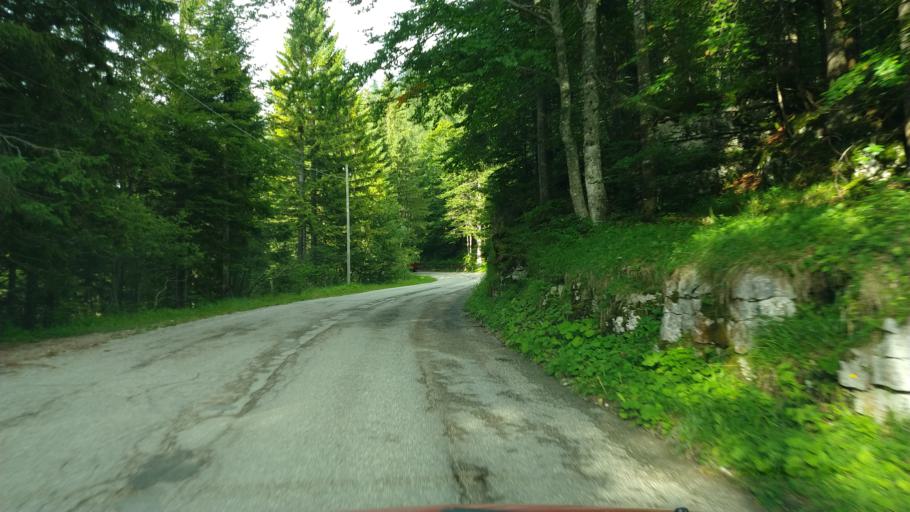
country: IT
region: Veneto
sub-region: Provincia di Vicenza
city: Lastebasse
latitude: 45.8934
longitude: 11.2686
